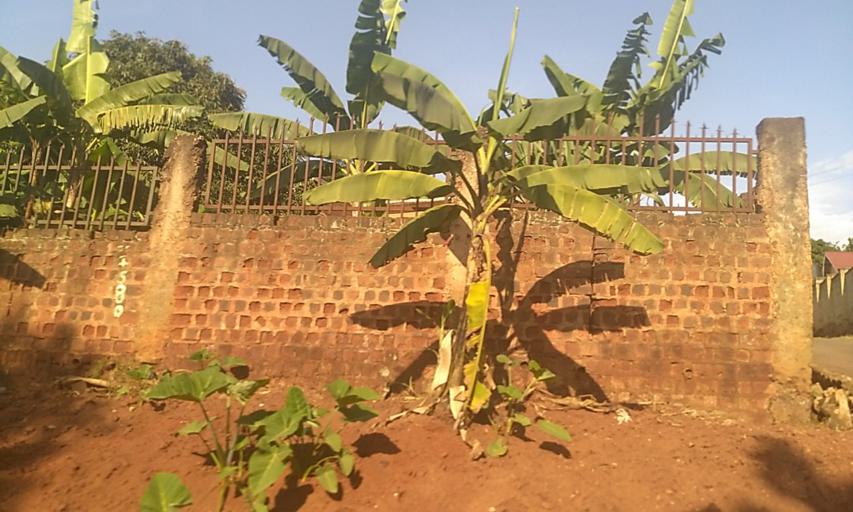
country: UG
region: Central Region
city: Kampala Central Division
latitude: 0.3132
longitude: 32.5553
